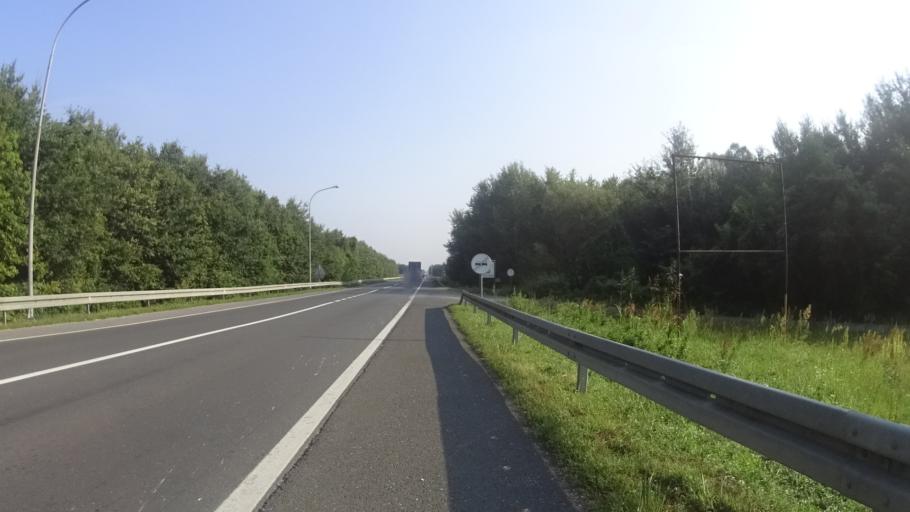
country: HR
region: Varazdinska
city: Varazdin
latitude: 46.3242
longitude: 16.3591
